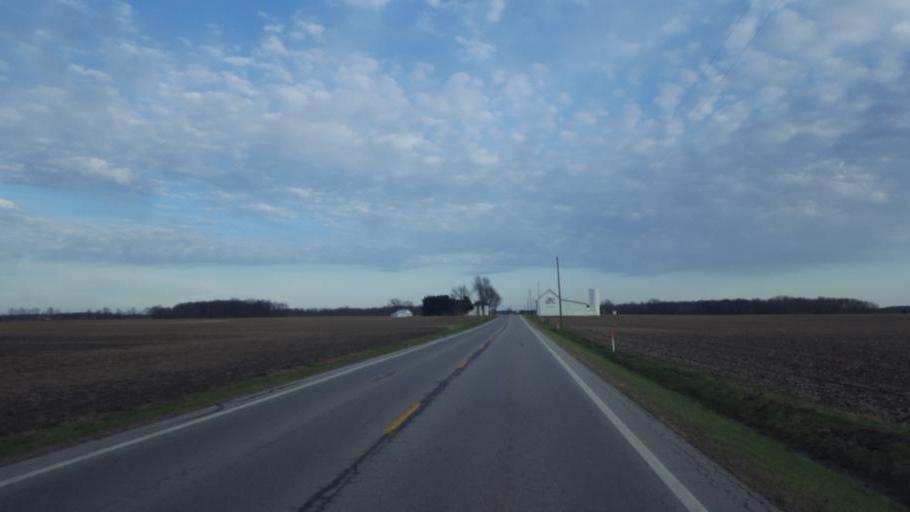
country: US
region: Ohio
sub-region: Morrow County
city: Mount Gilead
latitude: 40.5744
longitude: -82.8921
